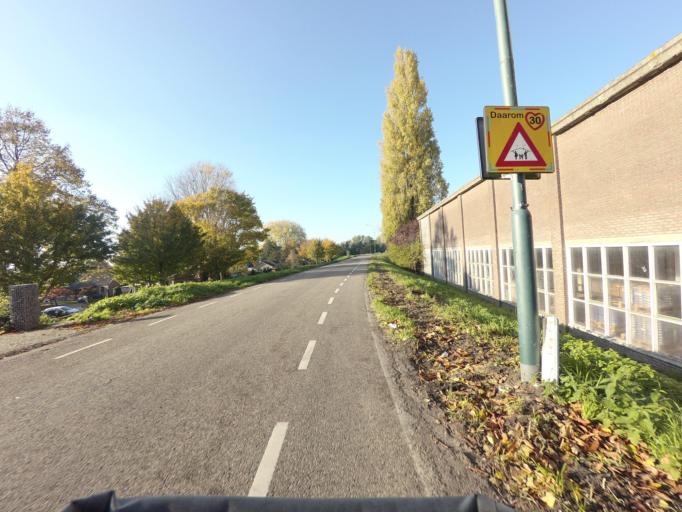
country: NL
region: North Brabant
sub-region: Gemeente Woudrichem
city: Woudrichem
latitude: 51.7870
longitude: 5.0542
